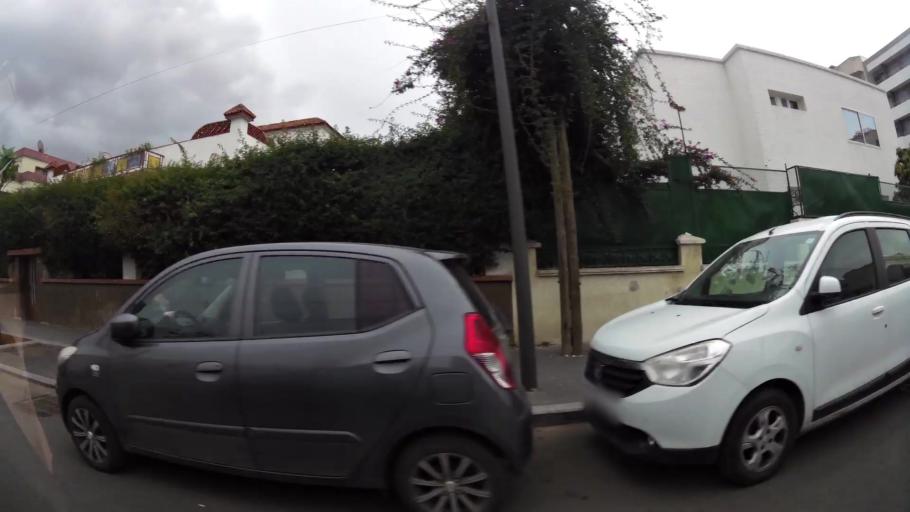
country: MA
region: Grand Casablanca
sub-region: Casablanca
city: Casablanca
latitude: 33.5693
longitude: -7.6243
